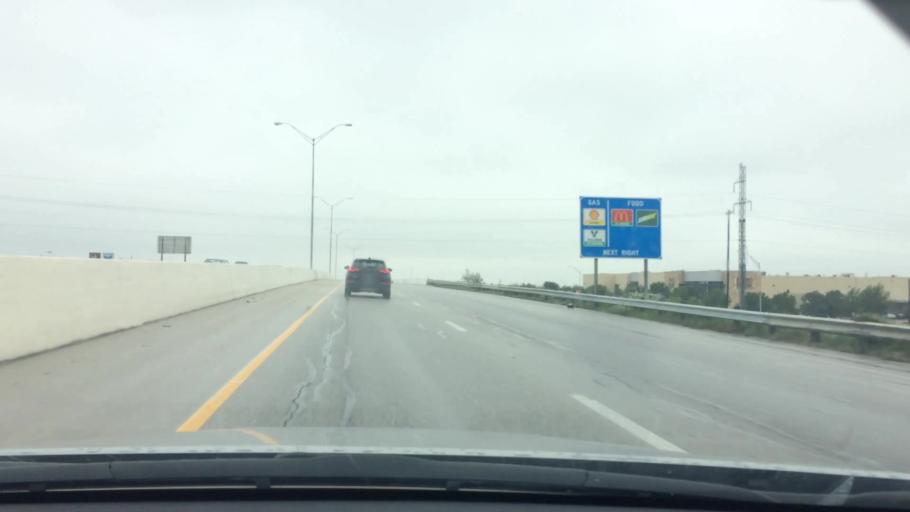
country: US
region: Texas
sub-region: Bexar County
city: Lackland Air Force Base
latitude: 29.4204
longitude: -98.5913
